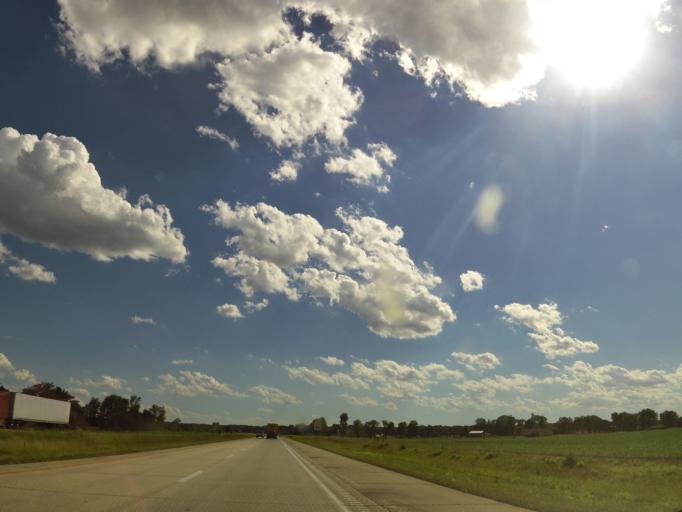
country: US
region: Illinois
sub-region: Hancock County
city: Warsaw
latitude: 40.3861
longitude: -91.5772
